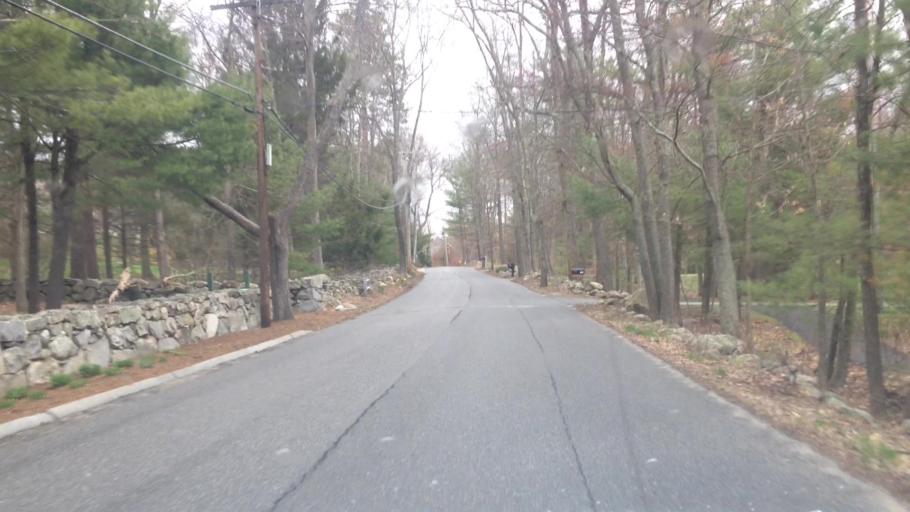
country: US
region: Massachusetts
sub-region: Middlesex County
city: Acton
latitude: 42.4924
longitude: -71.4051
